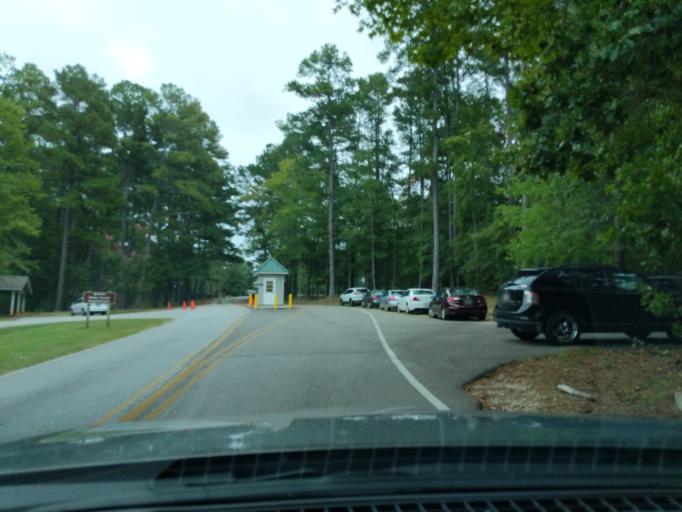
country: US
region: Georgia
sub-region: Columbia County
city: Appling
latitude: 33.6432
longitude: -82.3855
